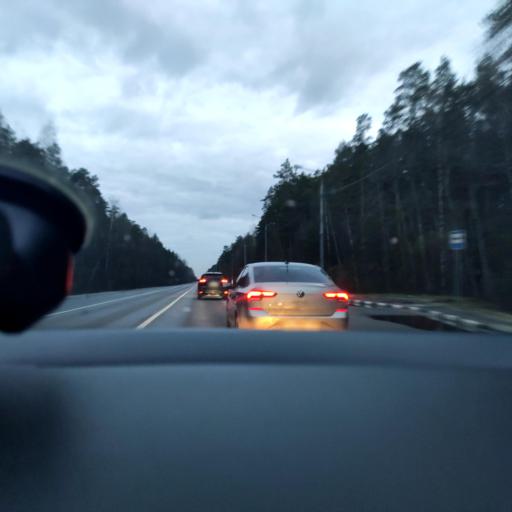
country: RU
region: Moskovskaya
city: Il'inskiy Pogost
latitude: 55.4593
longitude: 38.9860
